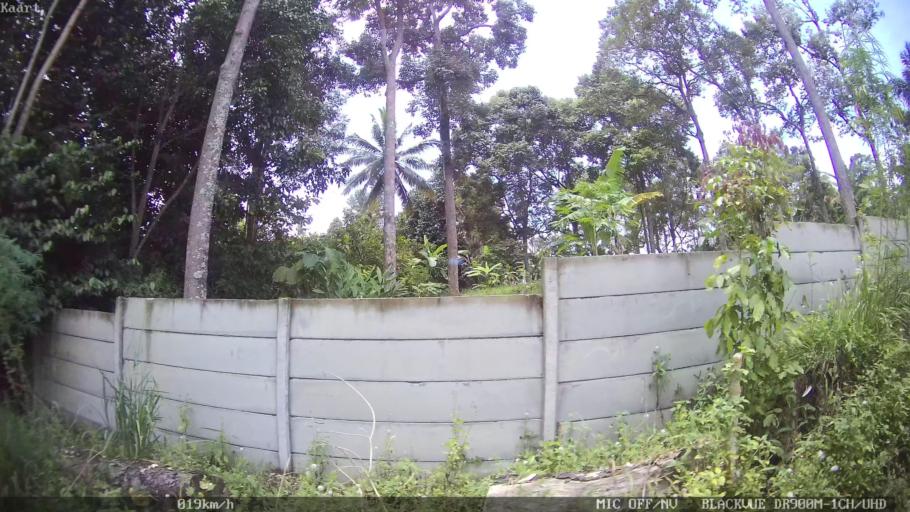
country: ID
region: Lampung
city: Bandarlampung
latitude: -5.4119
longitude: 105.2138
